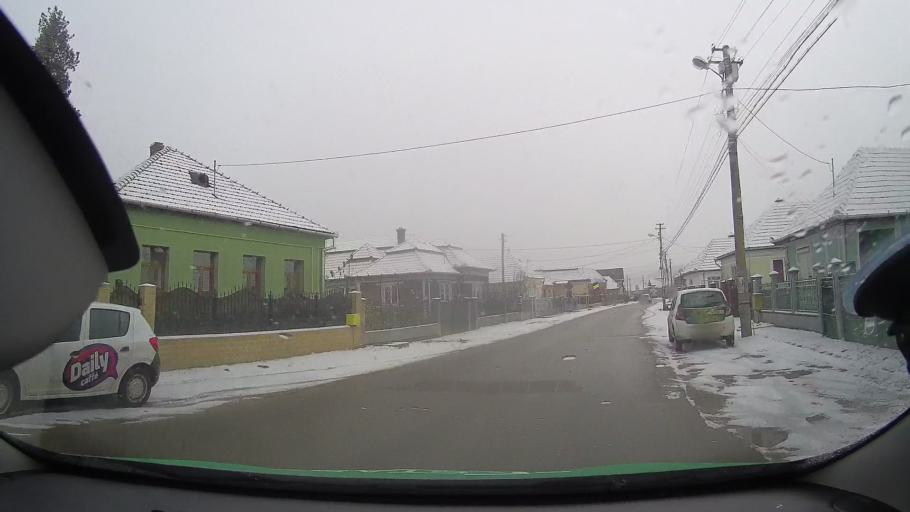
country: RO
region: Alba
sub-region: Municipiul Aiud
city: Ciumbrud
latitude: 46.3077
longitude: 23.7610
